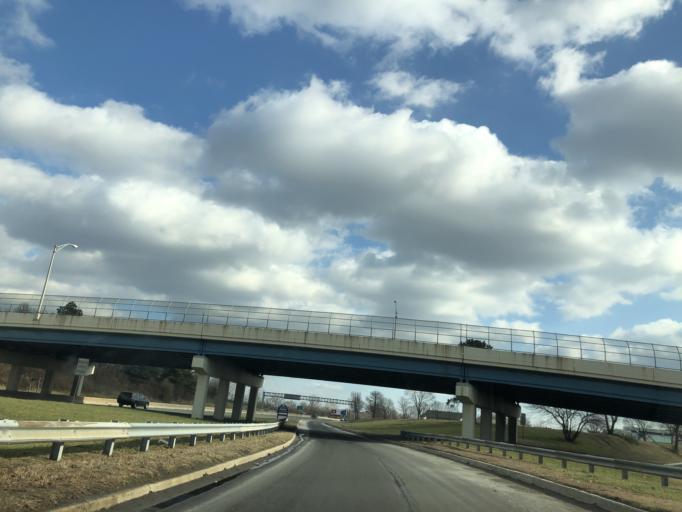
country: US
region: New Jersey
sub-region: Camden County
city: Camden
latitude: 39.9457
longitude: -75.1139
